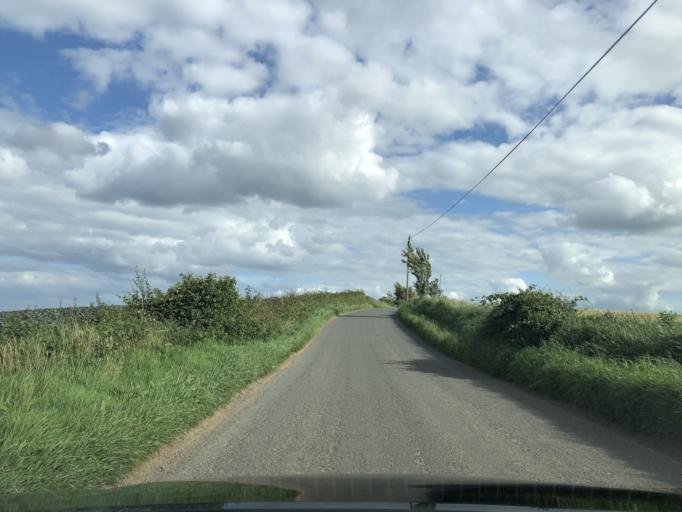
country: GB
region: Northern Ireland
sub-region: Ards District
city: Newtownards
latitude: 54.5638
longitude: -5.7108
